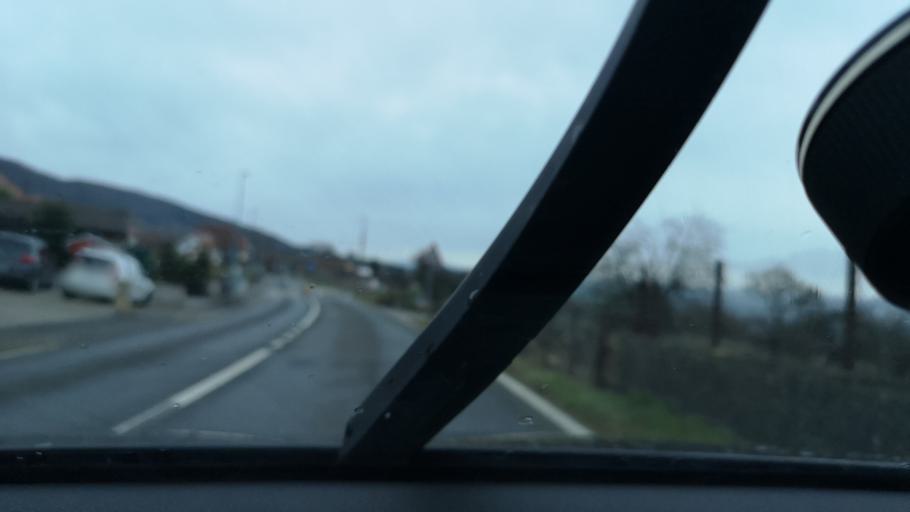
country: CH
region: Vaud
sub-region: Jura-Nord vaudois District
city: Yvonand
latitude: 46.8468
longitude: 6.7084
